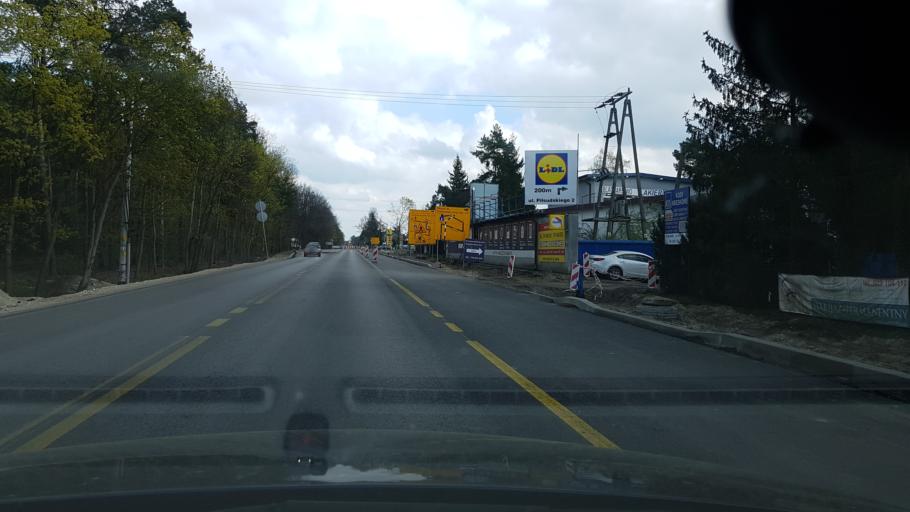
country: PL
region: Masovian Voivodeship
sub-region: Powiat minski
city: Sulejowek
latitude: 52.2525
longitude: 21.2655
